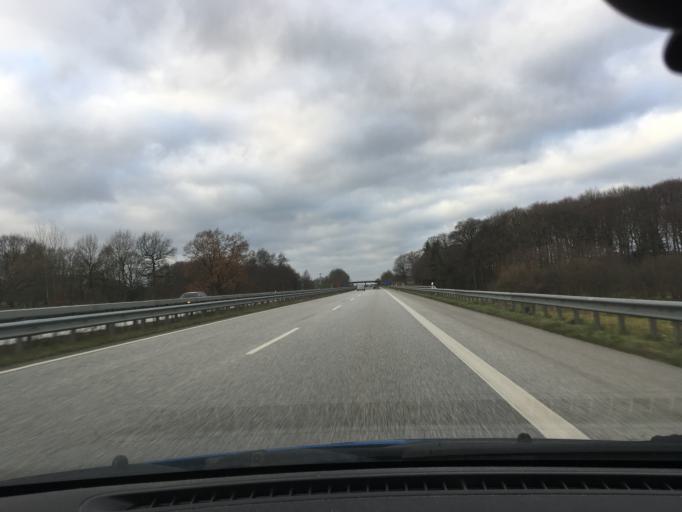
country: DE
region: Schleswig-Holstein
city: Agethorst
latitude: 54.0334
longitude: 9.4357
